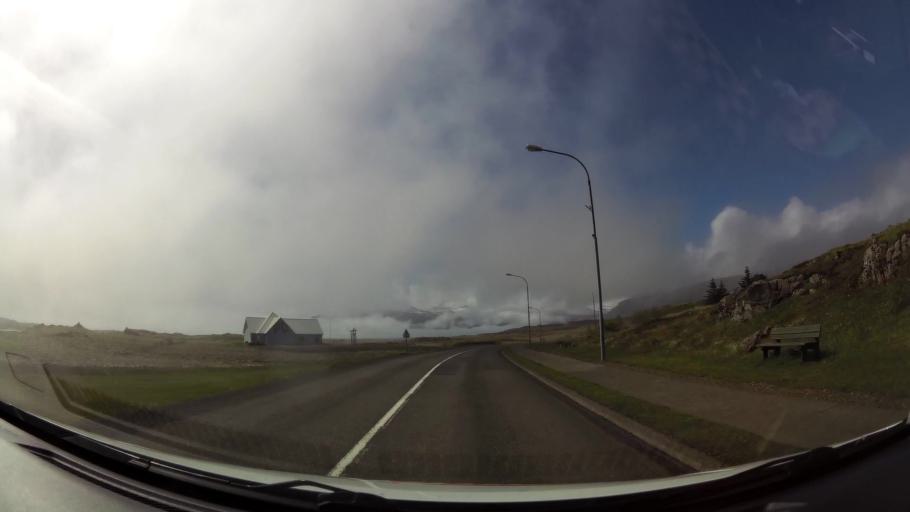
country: IS
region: East
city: Reydarfjoerdur
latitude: 64.6540
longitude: -14.2961
